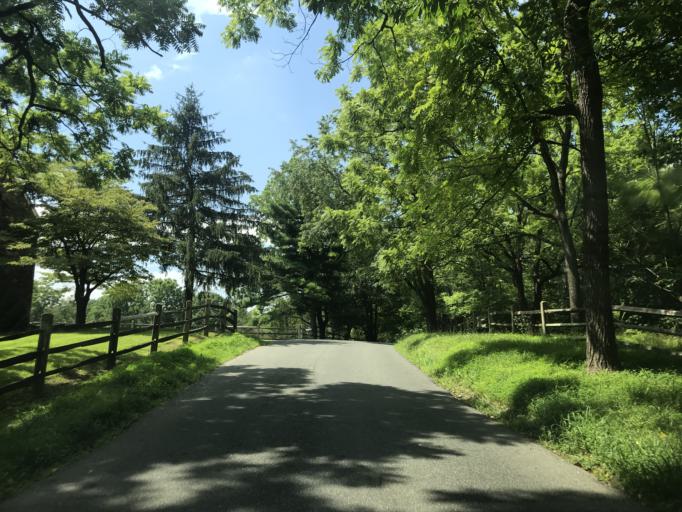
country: US
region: Delaware
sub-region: New Castle County
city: Hockessin
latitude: 39.7891
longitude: -75.6542
